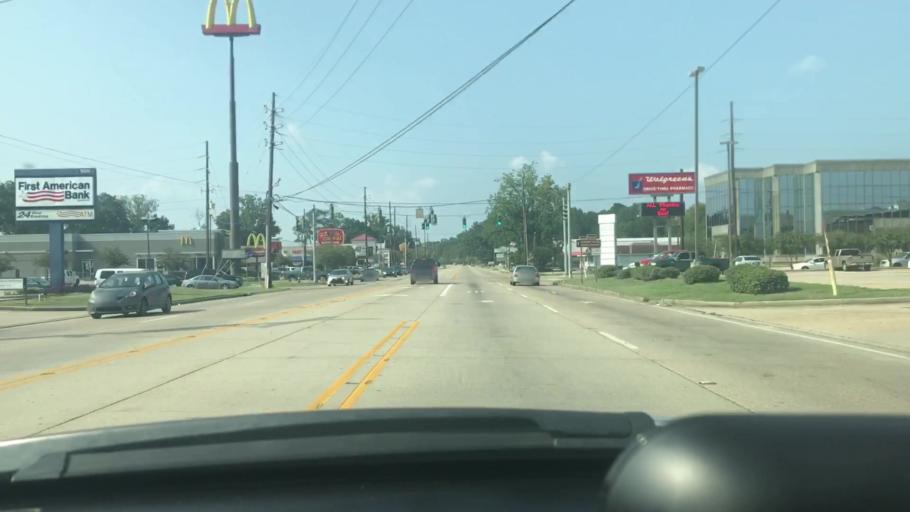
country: US
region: Louisiana
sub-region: Tangipahoa Parish
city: Hammond
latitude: 30.4839
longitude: -90.4569
